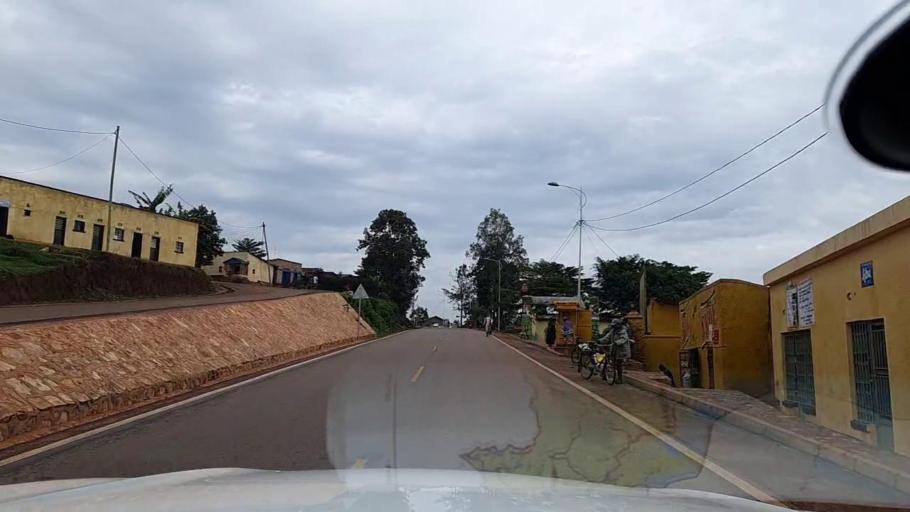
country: RW
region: Southern Province
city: Butare
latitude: -2.5830
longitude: 29.7367
